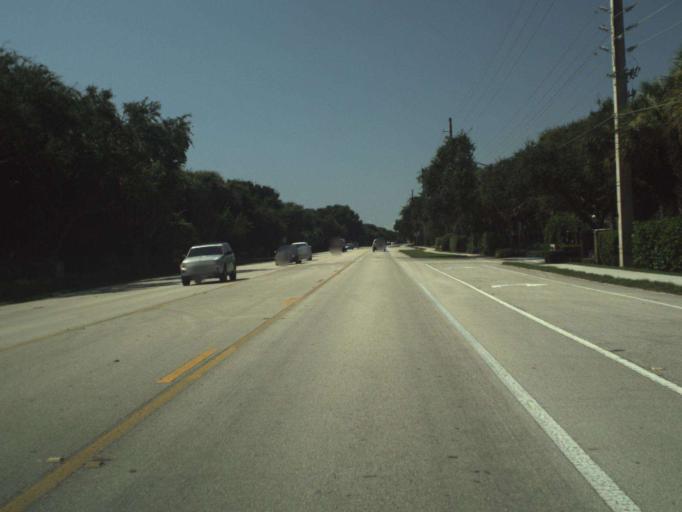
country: US
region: Florida
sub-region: Indian River County
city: Indian River Shores
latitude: 27.6891
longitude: -80.3698
